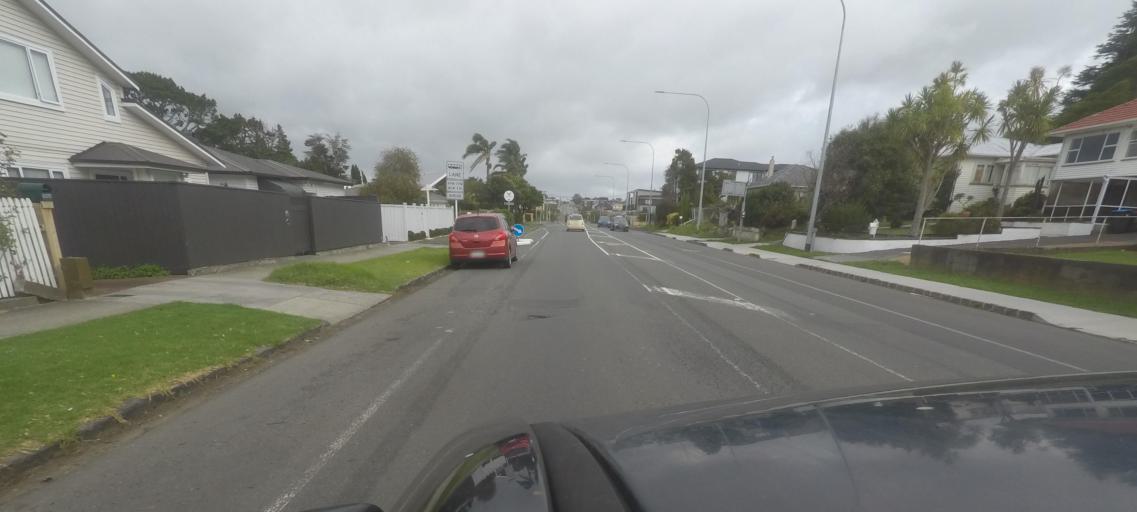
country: NZ
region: Auckland
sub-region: Auckland
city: Auckland
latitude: -36.9127
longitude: 174.7391
